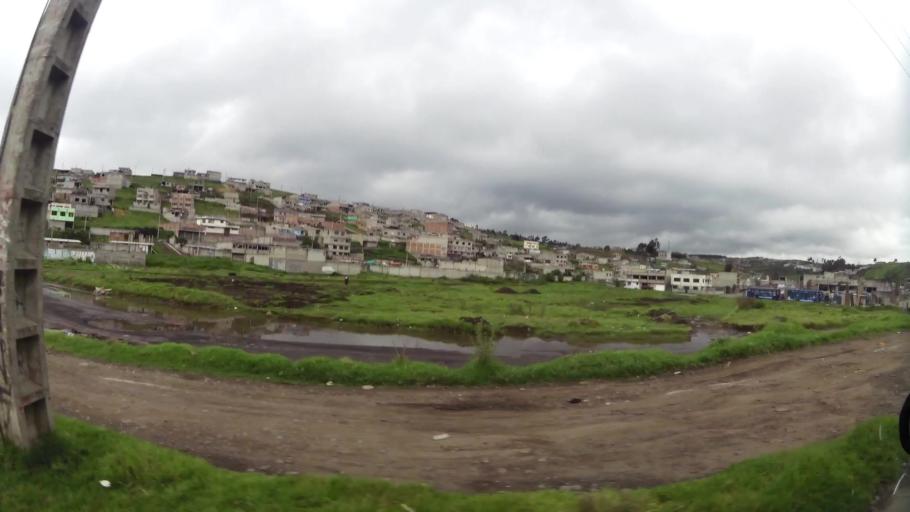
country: EC
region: Pichincha
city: Sangolqui
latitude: -0.3157
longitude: -78.5289
